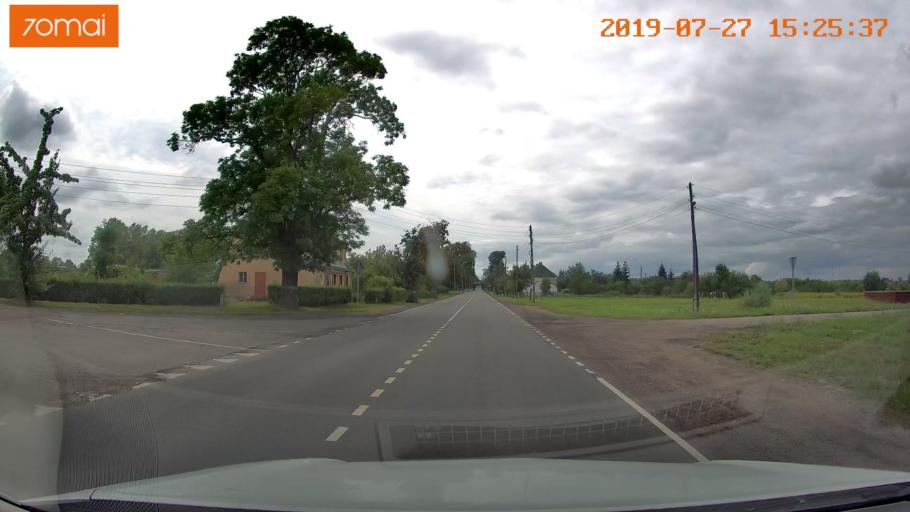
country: RU
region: Kaliningrad
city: Nesterov
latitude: 54.6315
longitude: 22.5861
